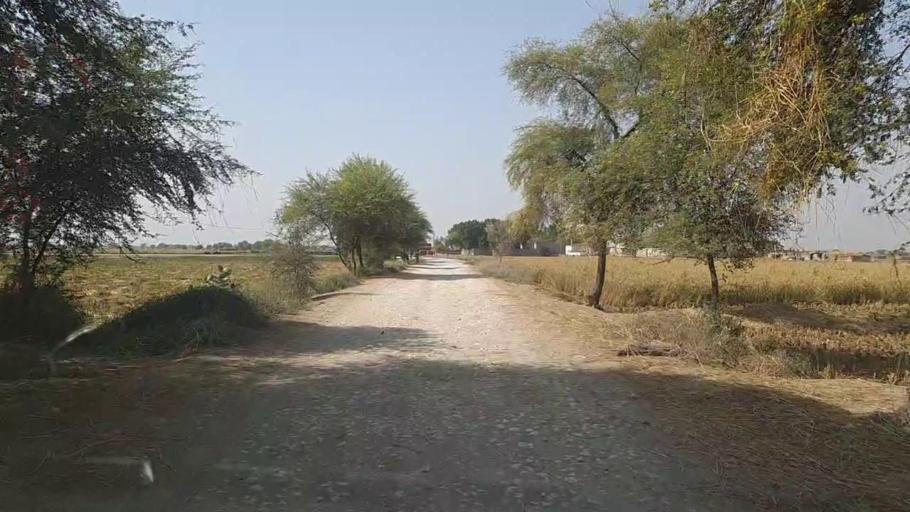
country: PK
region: Sindh
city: Kandhkot
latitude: 28.3954
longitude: 69.2954
